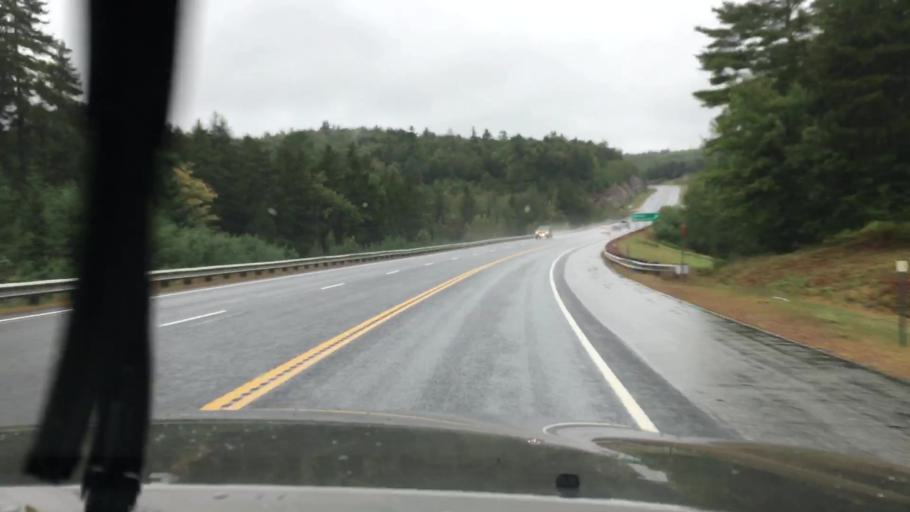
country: US
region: New Hampshire
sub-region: Cheshire County
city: Harrisville
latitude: 43.0047
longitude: -72.1551
